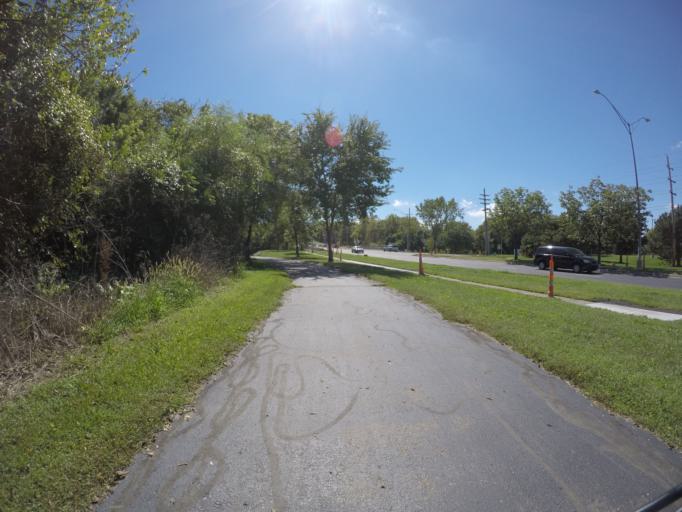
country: US
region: Kansas
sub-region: Johnson County
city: Olathe
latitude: 38.8953
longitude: -94.7607
